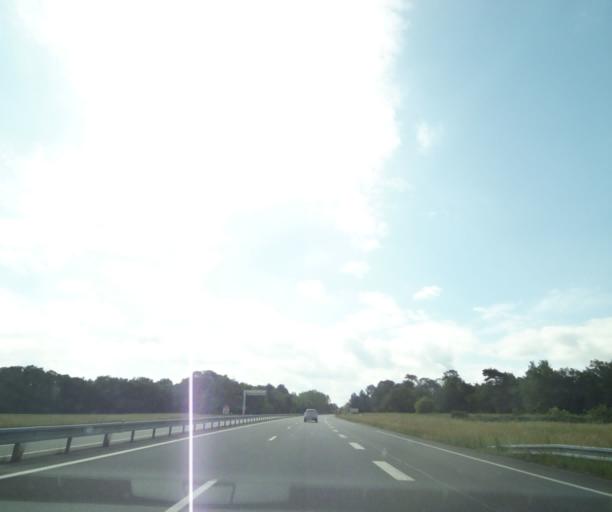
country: FR
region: Pays de la Loire
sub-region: Departement de Maine-et-Loire
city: Jumelles
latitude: 47.4171
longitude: -0.1299
